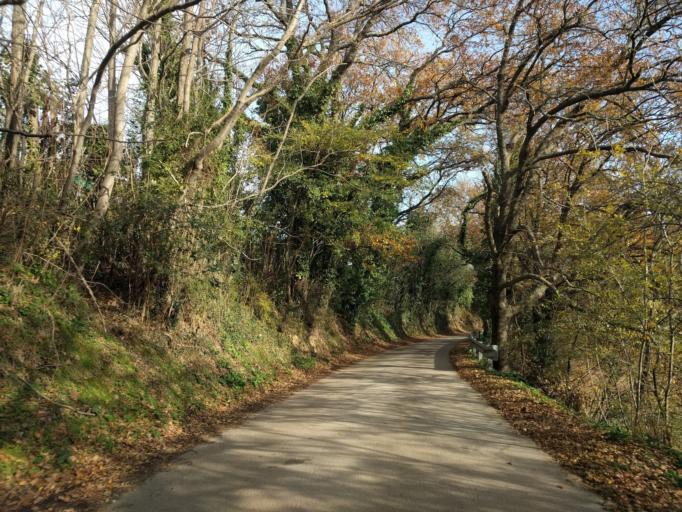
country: IT
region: The Marches
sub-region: Provincia di Pesaro e Urbino
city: Cuccurano
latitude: 43.8152
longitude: 12.9681
